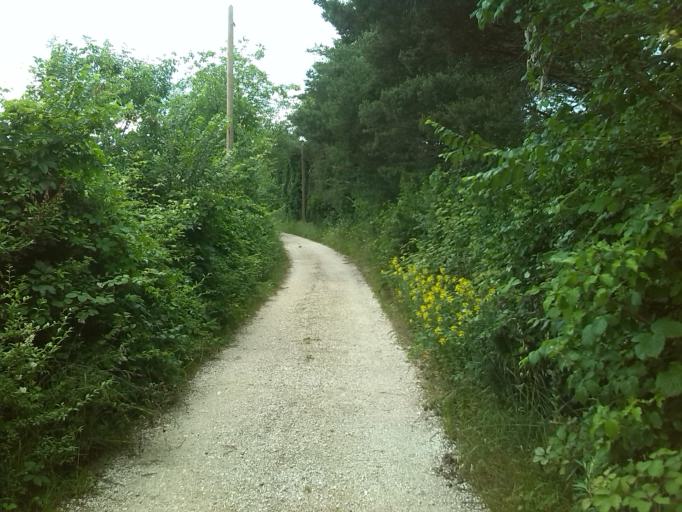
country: IT
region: Friuli Venezia Giulia
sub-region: Provincia di Udine
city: Cividale del Friuli
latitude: 46.0968
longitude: 13.4507
